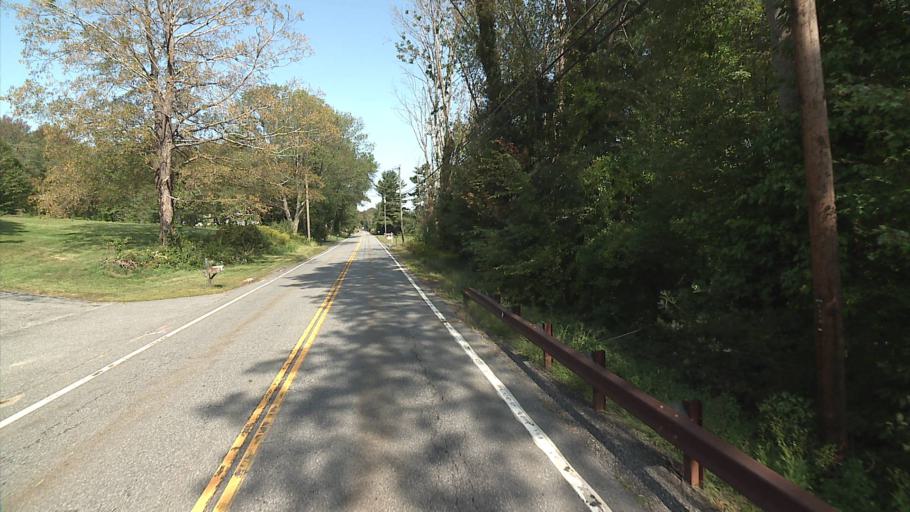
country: US
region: Connecticut
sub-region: Windham County
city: South Woodstock
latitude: 41.9755
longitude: -71.9915
